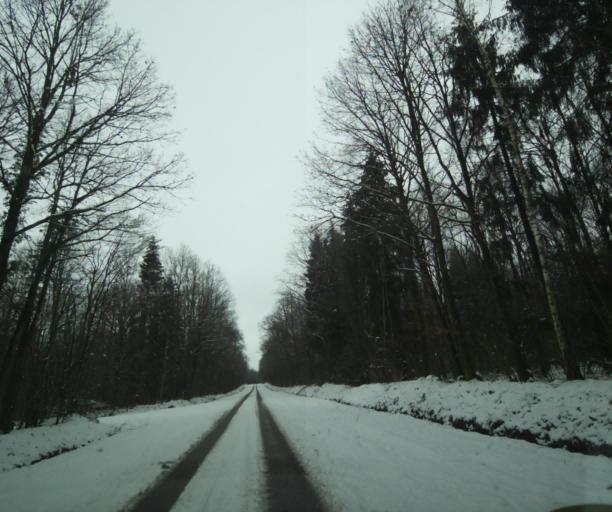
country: FR
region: Champagne-Ardenne
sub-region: Departement de la Haute-Marne
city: Montier-en-Der
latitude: 48.4208
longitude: 4.7704
